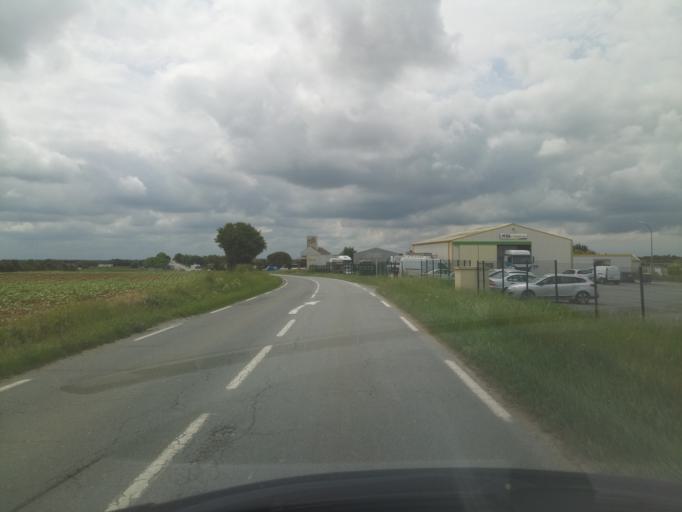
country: FR
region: Poitou-Charentes
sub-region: Departement de la Charente-Maritime
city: Saint-Jean-de-Liversay
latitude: 46.2318
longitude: -0.8806
